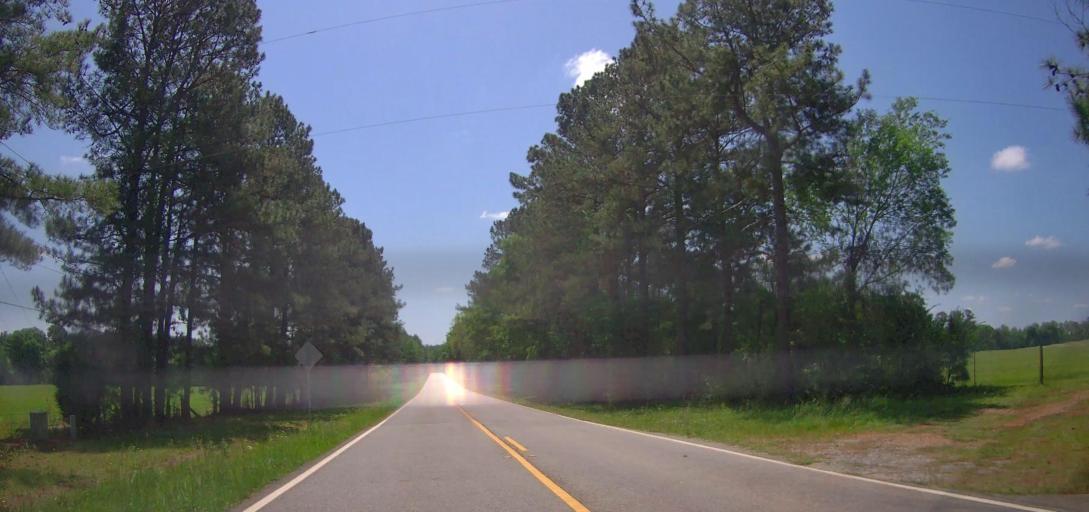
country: US
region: Georgia
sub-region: Jones County
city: Gray
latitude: 33.0143
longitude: -83.5632
